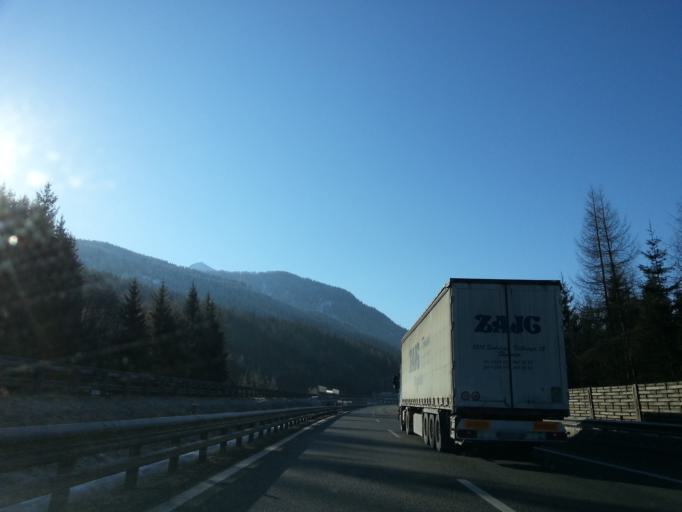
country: AT
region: Salzburg
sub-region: Politischer Bezirk Sankt Johann im Pongau
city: Flachau
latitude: 47.3624
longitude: 13.3971
